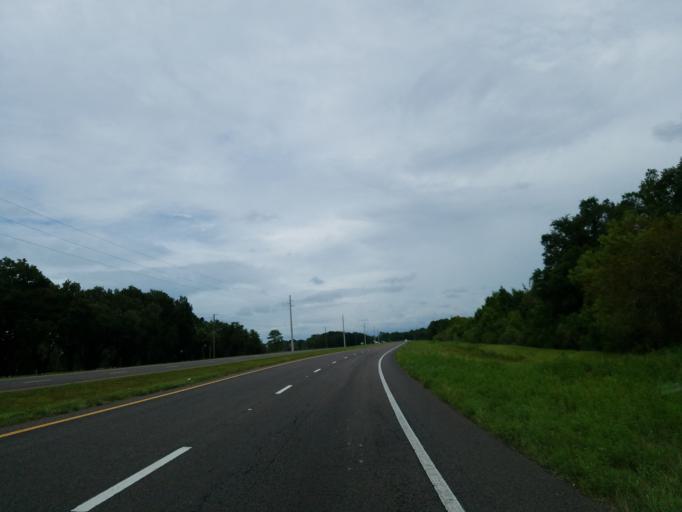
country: US
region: Florida
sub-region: Sumter County
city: Wildwood
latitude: 28.8610
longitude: -82.1631
